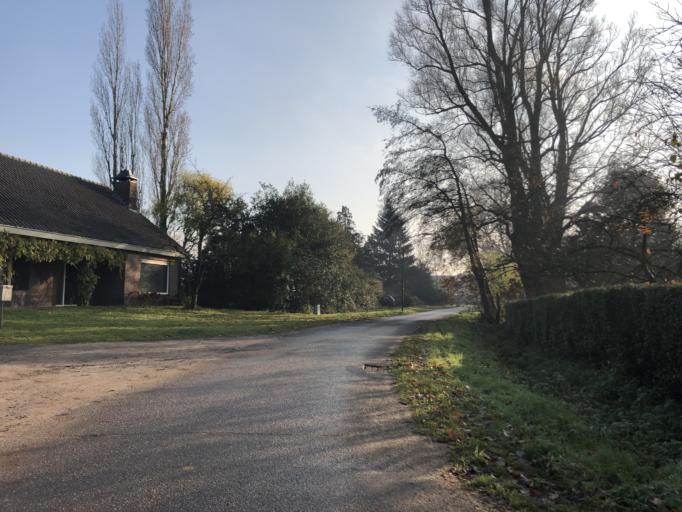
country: NL
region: North Brabant
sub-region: Gemeente Oosterhout
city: Oosterhout
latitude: 51.5941
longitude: 4.8465
